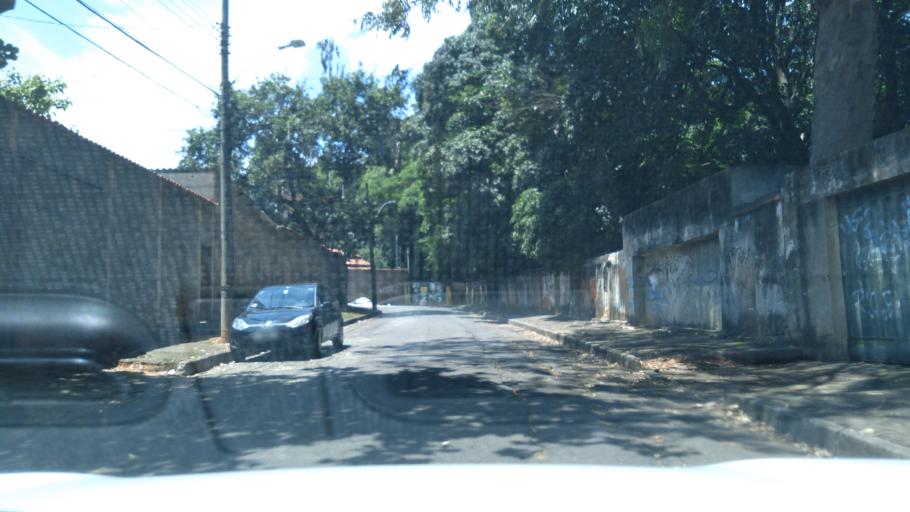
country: BR
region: Minas Gerais
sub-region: Contagem
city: Contagem
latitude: -19.8998
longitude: -44.0164
